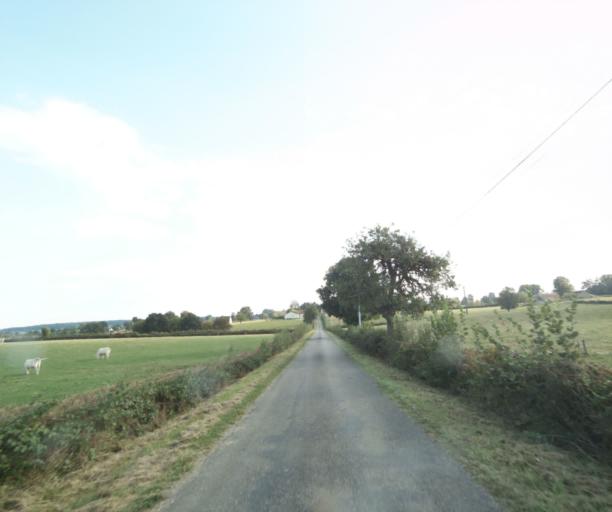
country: FR
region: Bourgogne
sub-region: Departement de Saone-et-Loire
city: Paray-le-Monial
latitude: 46.5277
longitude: 4.1218
